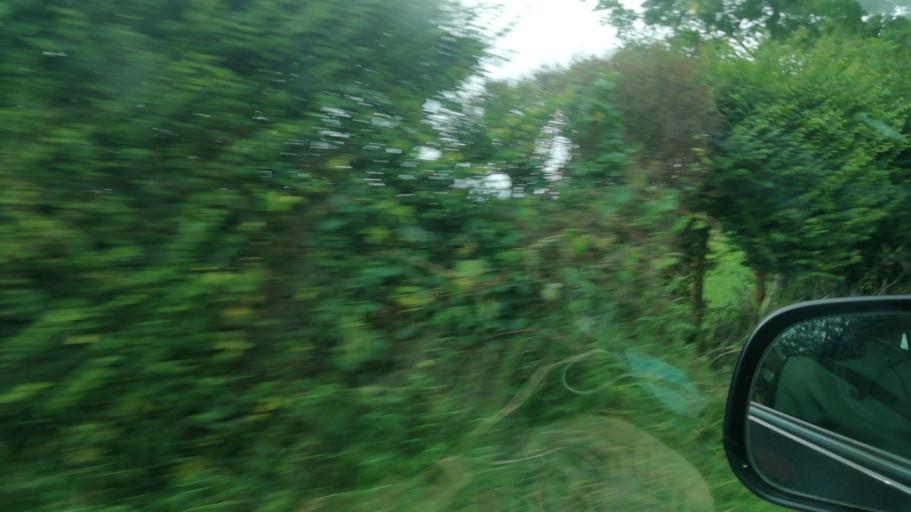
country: IE
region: Munster
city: Fethard
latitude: 52.5582
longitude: -7.5634
